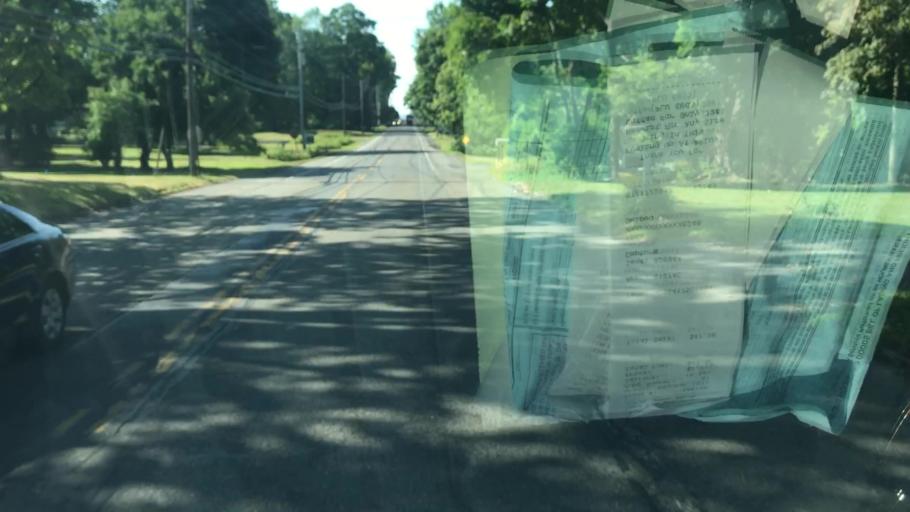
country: US
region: New York
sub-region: Onondaga County
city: Skaneateles
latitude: 42.9376
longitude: -76.4110
